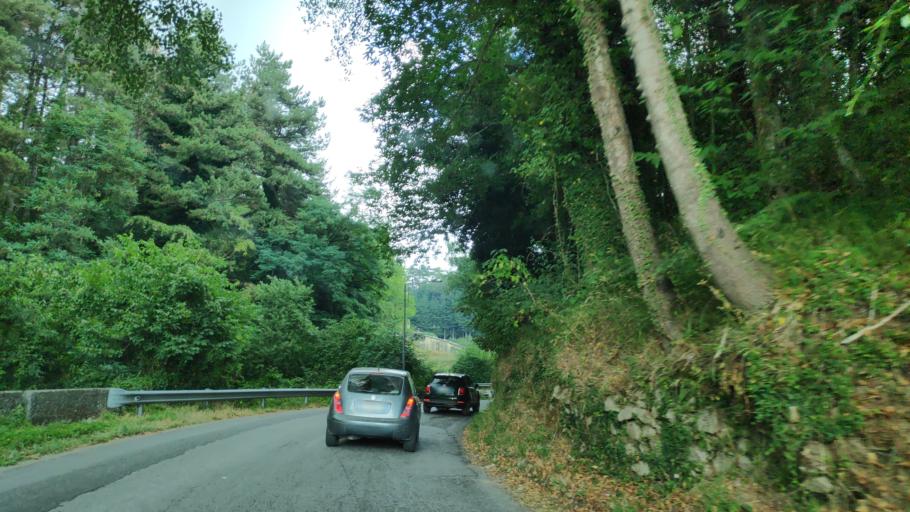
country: IT
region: Calabria
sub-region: Provincia di Vibo-Valentia
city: Mongiana
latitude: 38.5181
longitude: 16.3210
